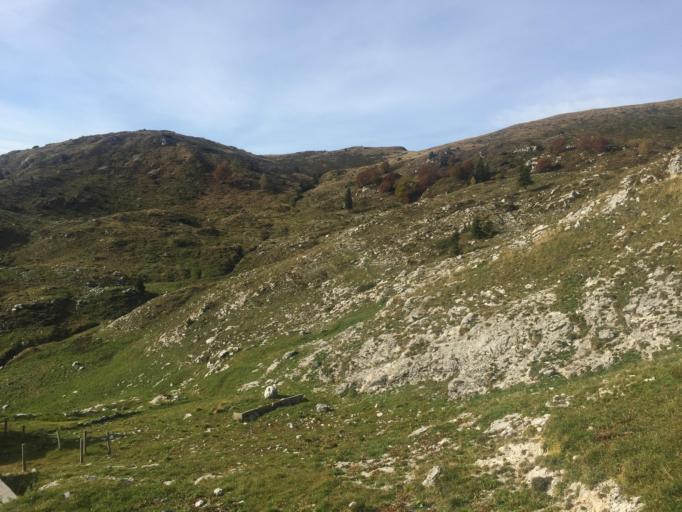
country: IT
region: Friuli Venezia Giulia
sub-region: Provincia di Udine
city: Preone
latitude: 46.3363
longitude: 12.8463
